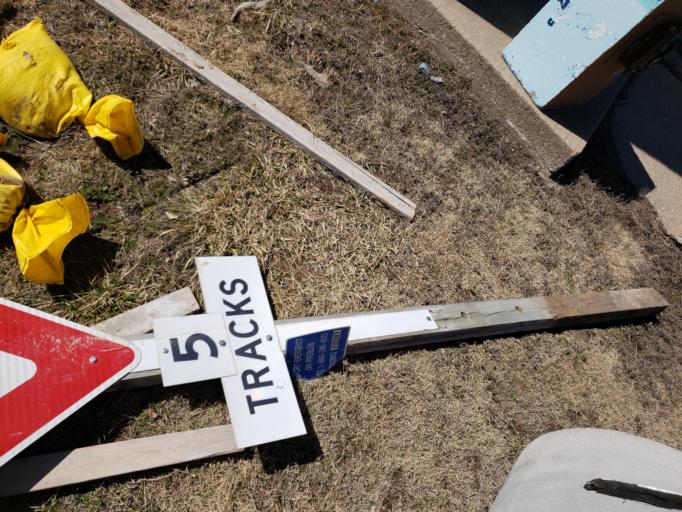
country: US
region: Kansas
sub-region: Ness County
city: Ness City
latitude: 38.4523
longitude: -99.9024
